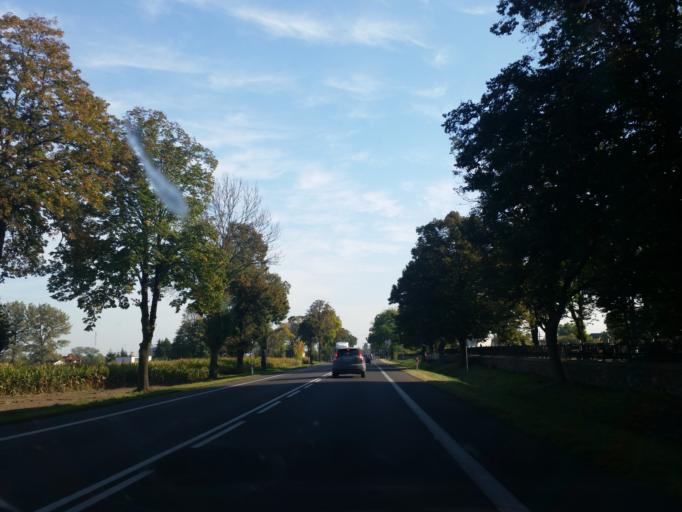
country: PL
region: Masovian Voivodeship
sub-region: Powiat plocki
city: Drobin
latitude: 52.7416
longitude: 19.9907
